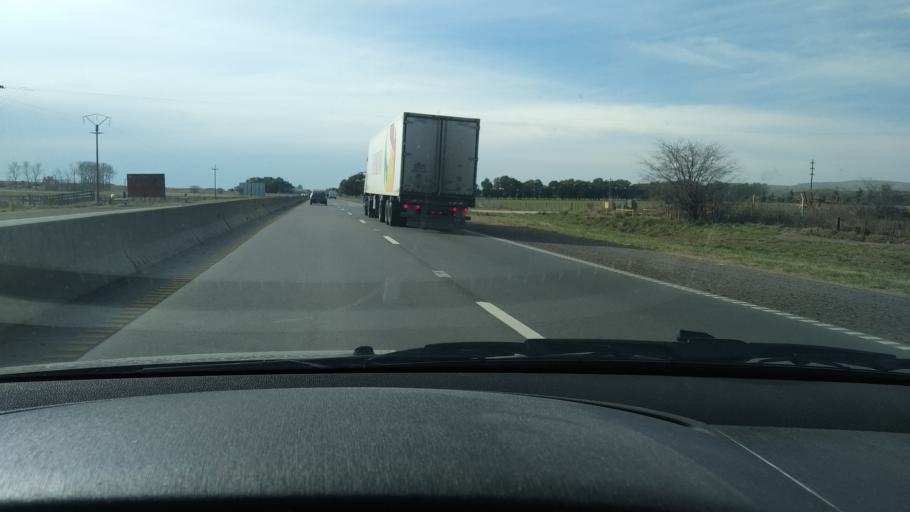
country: AR
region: Buenos Aires
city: Olavarria
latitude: -36.9250
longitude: -60.2153
